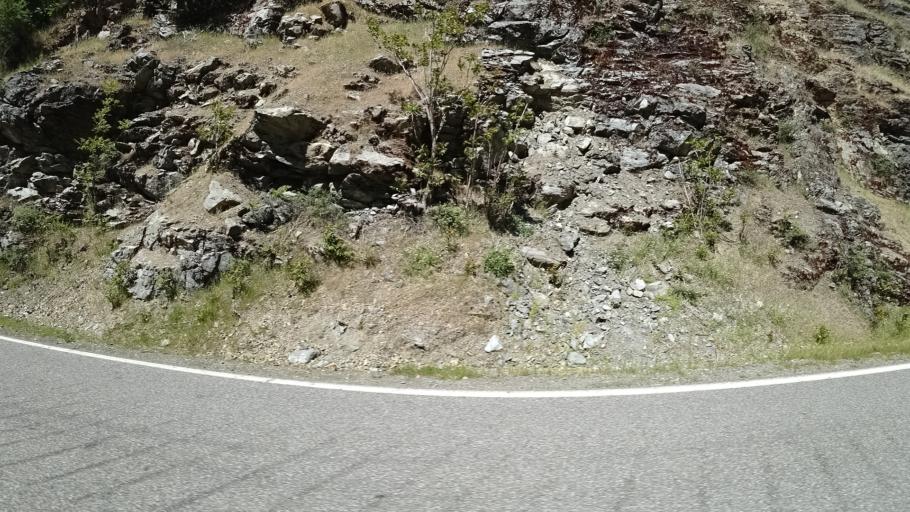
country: US
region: California
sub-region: Trinity County
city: Hayfork
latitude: 40.7518
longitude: -123.1604
